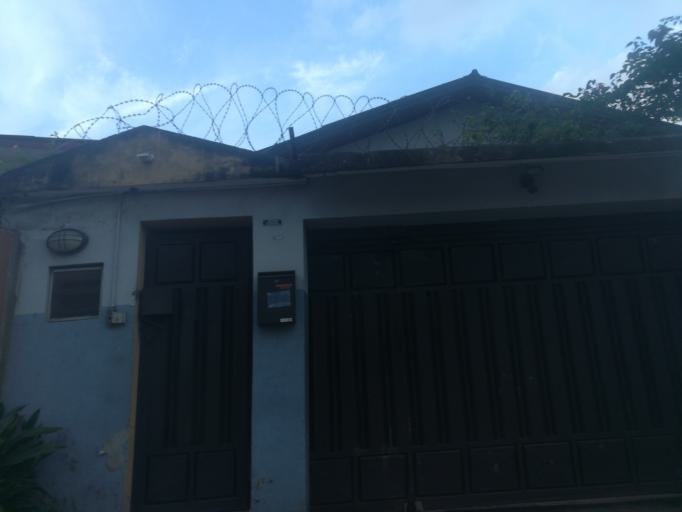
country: NG
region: Lagos
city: Somolu
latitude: 6.5557
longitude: 3.3852
